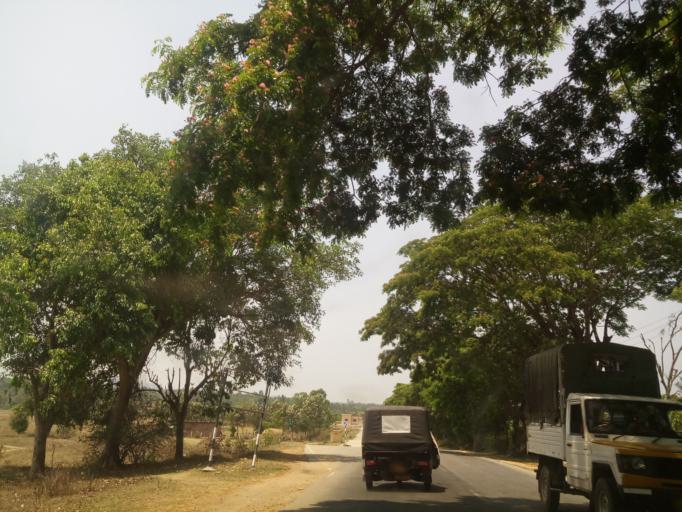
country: IN
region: Karnataka
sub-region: Hassan
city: Alur
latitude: 12.9513
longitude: 75.9703
